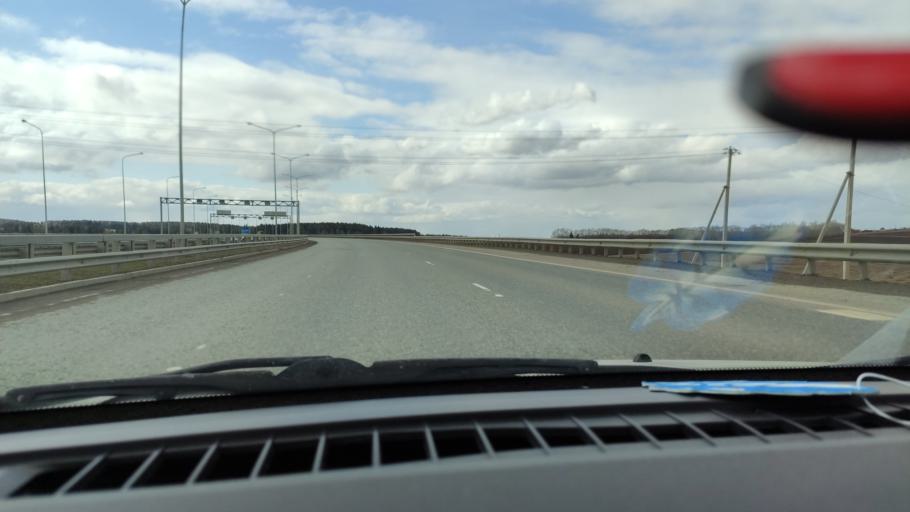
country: RU
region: Perm
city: Lobanovo
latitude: 57.8466
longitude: 56.2901
